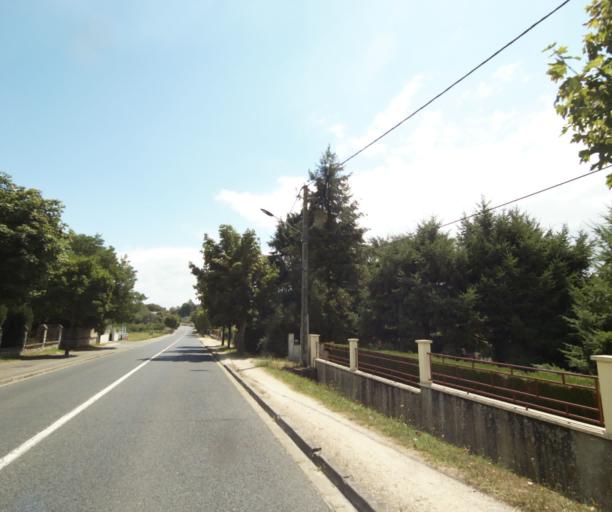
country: FR
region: Centre
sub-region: Departement du Loiret
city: Mardie
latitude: 47.8935
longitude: 2.0439
